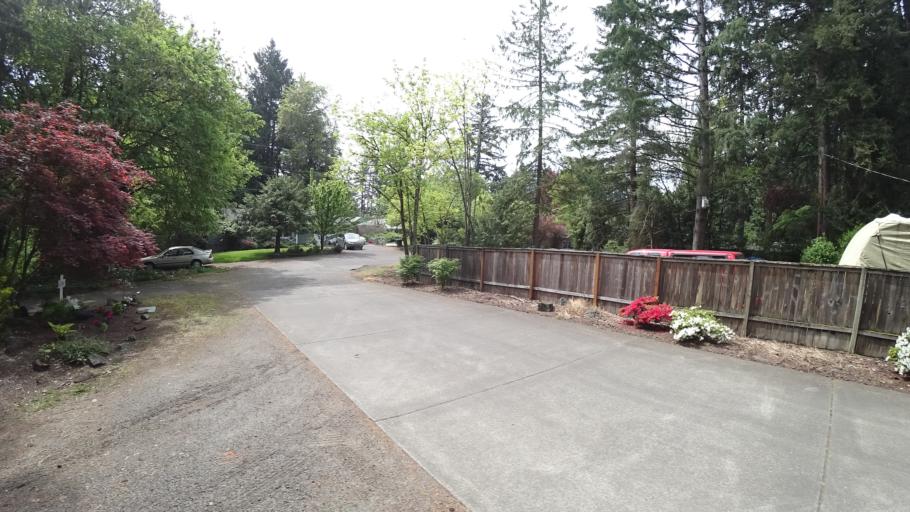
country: US
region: Oregon
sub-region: Washington County
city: Hillsboro
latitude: 45.5094
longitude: -122.9399
